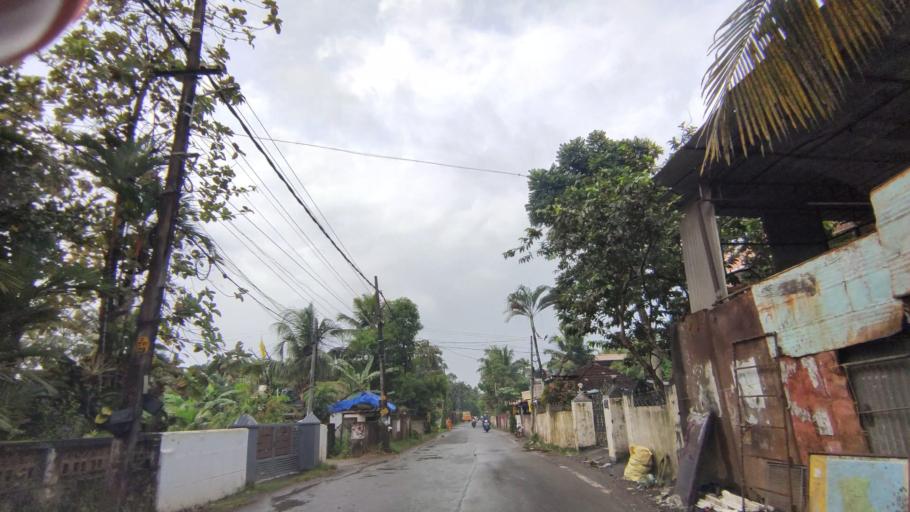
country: IN
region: Kerala
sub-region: Kottayam
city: Kottayam
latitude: 9.5796
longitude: 76.5029
